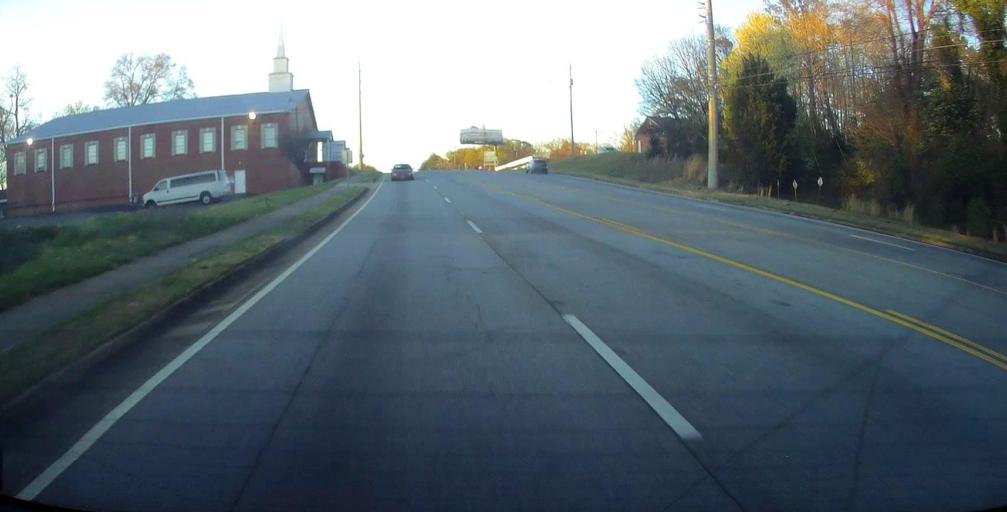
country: US
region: Alabama
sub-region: Russell County
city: Phenix City
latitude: 32.5046
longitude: -84.9899
